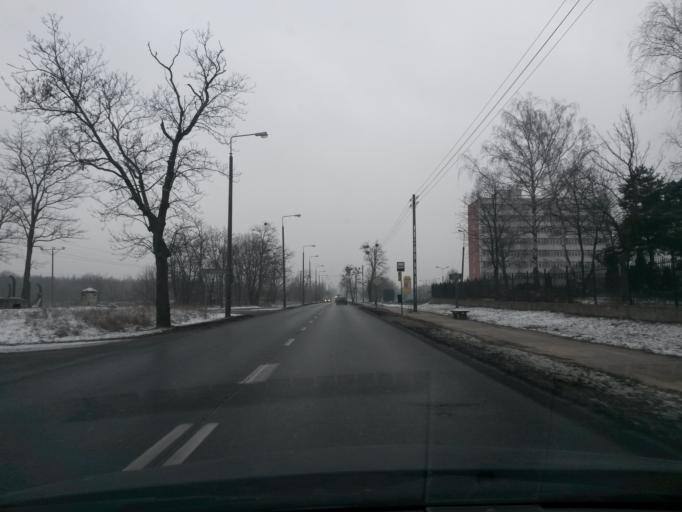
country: PL
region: Kujawsko-Pomorskie
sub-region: Torun
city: Torun
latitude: 52.9872
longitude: 18.5801
